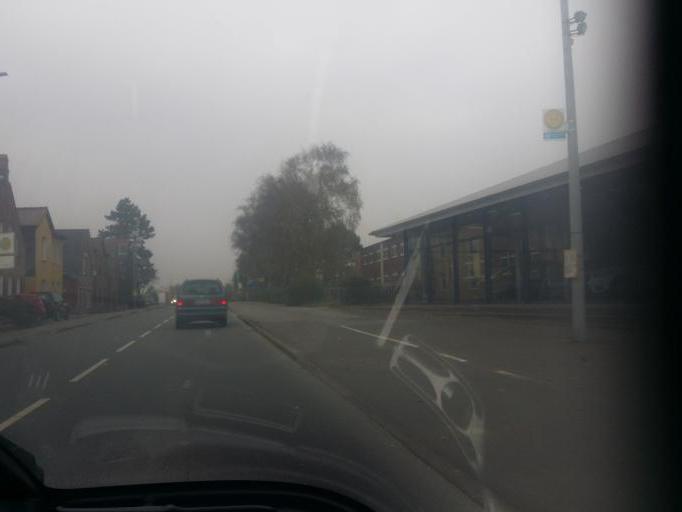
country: DE
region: Schleswig-Holstein
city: Husum
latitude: 54.4870
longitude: 9.0461
